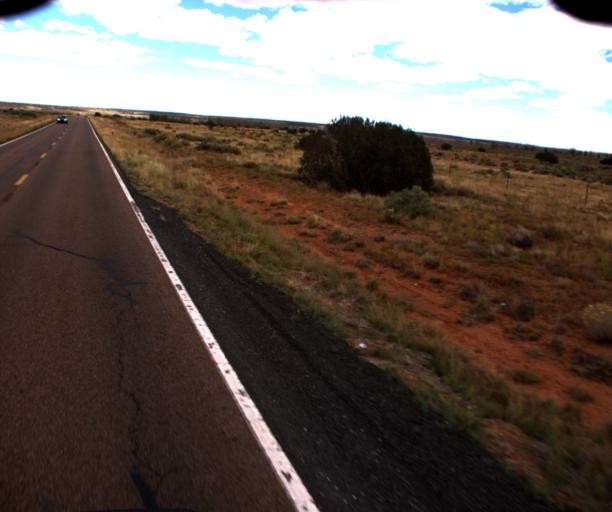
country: US
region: Arizona
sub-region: Navajo County
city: Heber-Overgaard
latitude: 34.6031
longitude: -110.3856
